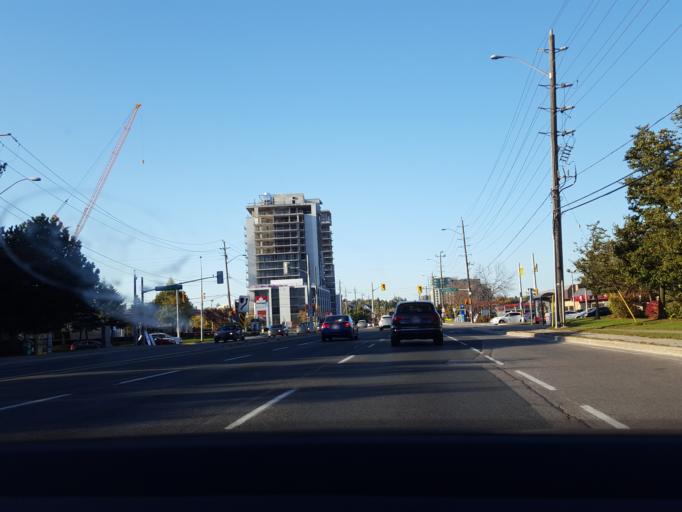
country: CA
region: Ontario
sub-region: York
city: Richmond Hill
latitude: 43.8595
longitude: -79.4344
